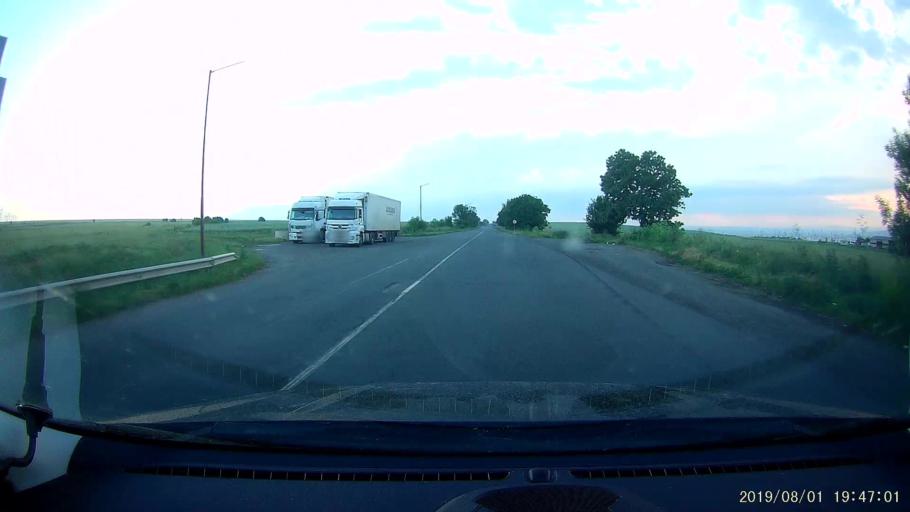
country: BG
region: Burgas
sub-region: Obshtina Karnobat
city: Karnobat
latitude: 42.6505
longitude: 26.9636
